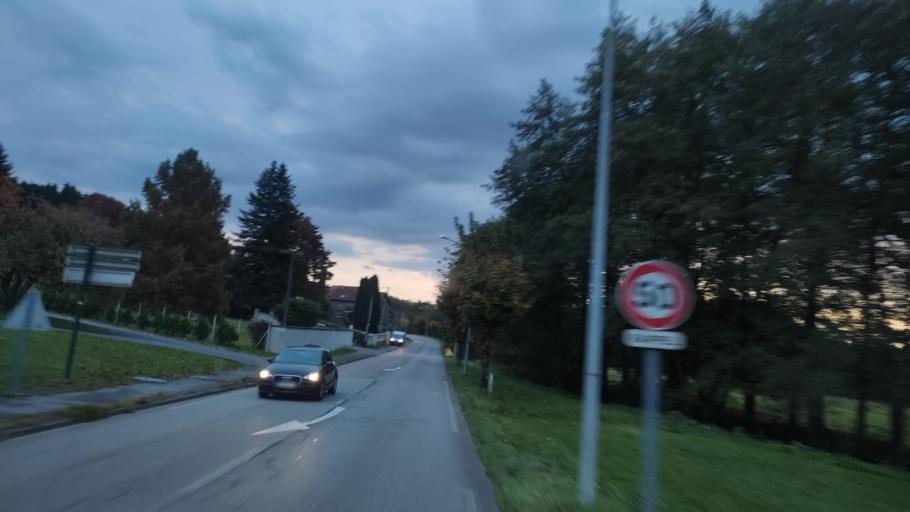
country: FR
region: Limousin
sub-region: Departement de la Haute-Vienne
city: Ambazac
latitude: 45.9606
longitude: 1.4067
